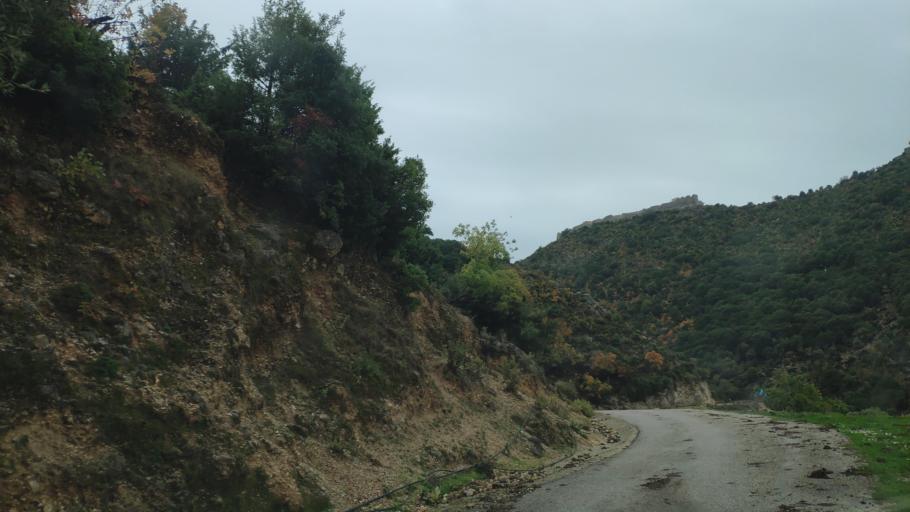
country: GR
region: Epirus
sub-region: Nomos Prevezis
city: Kanalaki
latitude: 39.3421
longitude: 20.6527
